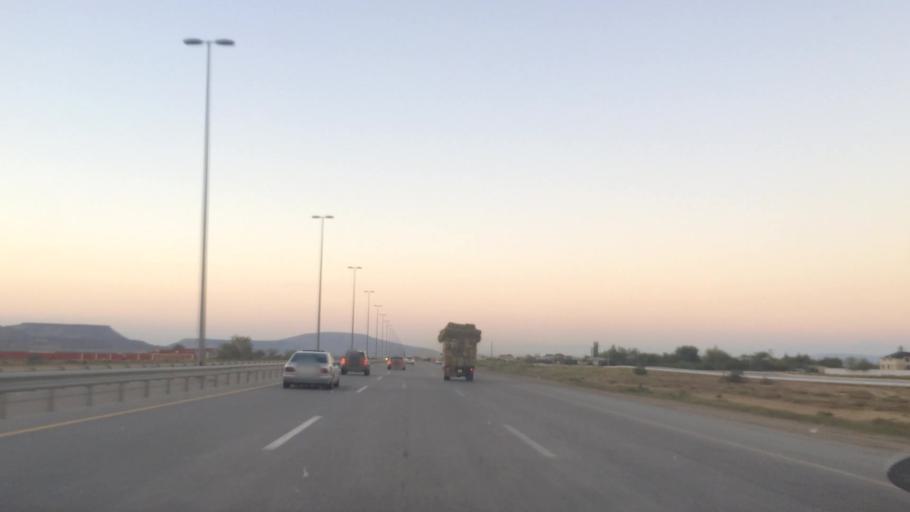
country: AZ
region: Baki
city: Qobustan
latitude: 40.0188
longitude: 49.4255
